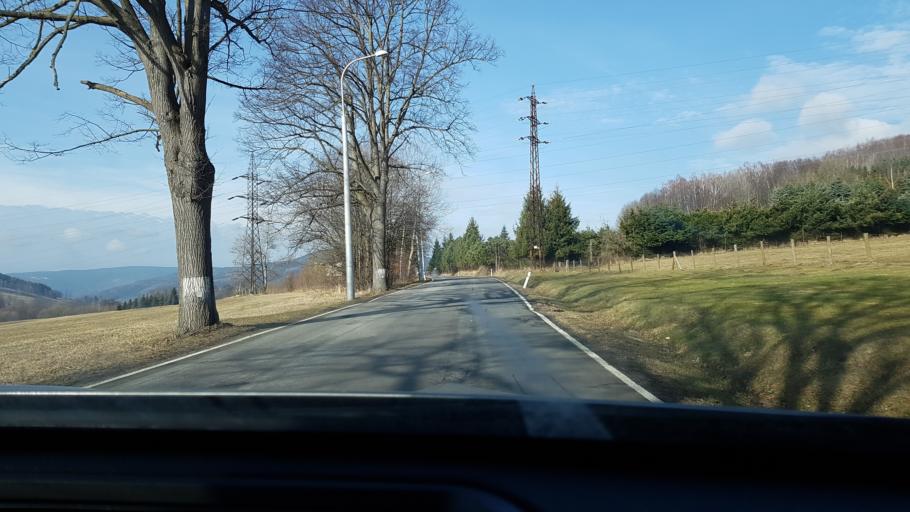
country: CZ
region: Olomoucky
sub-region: Okres Jesenik
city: Jesenik
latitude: 50.2274
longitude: 17.1797
